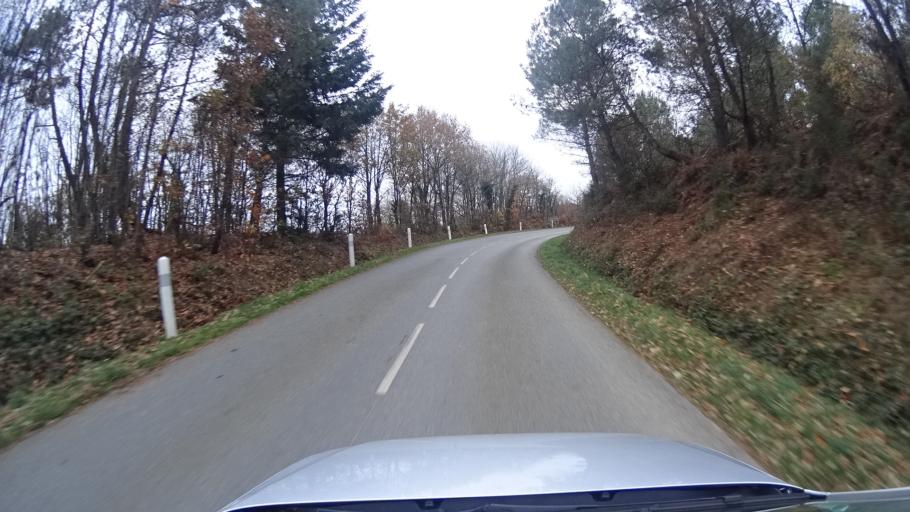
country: FR
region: Pays de la Loire
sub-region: Departement de la Loire-Atlantique
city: Avessac
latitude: 47.6561
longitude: -1.9536
